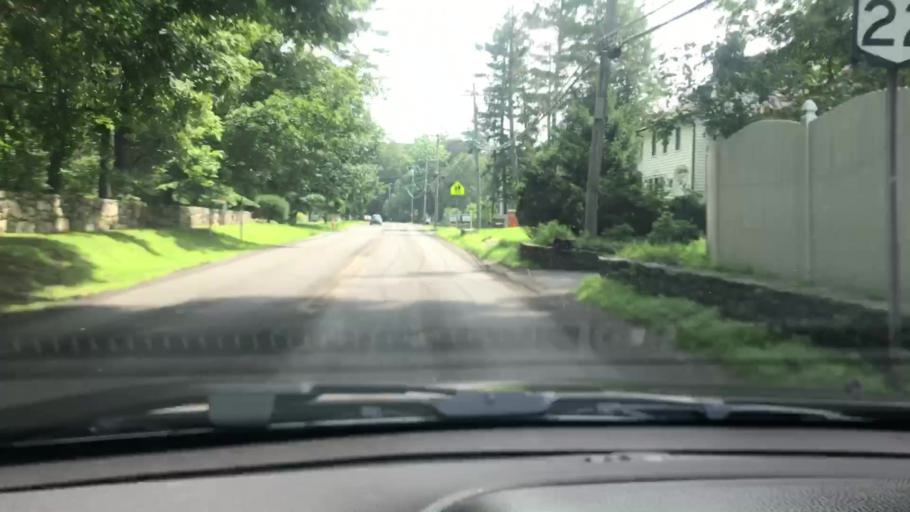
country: US
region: New York
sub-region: Westchester County
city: Bedford
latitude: 41.2189
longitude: -73.6574
